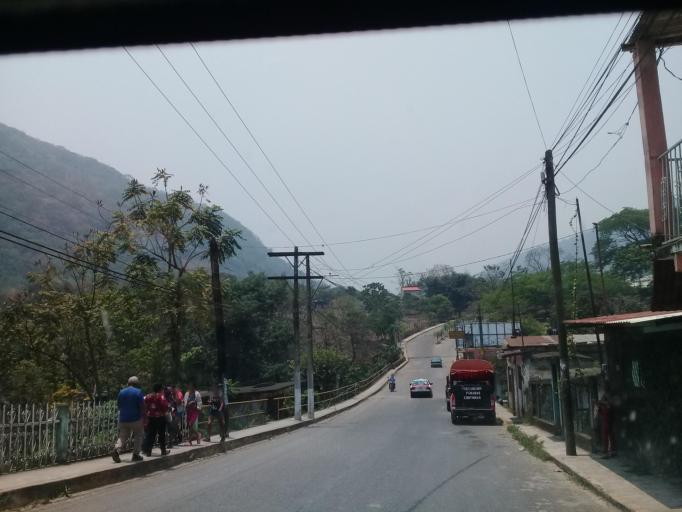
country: MX
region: Veracruz
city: Tezonapa
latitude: 18.6063
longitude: -96.6884
